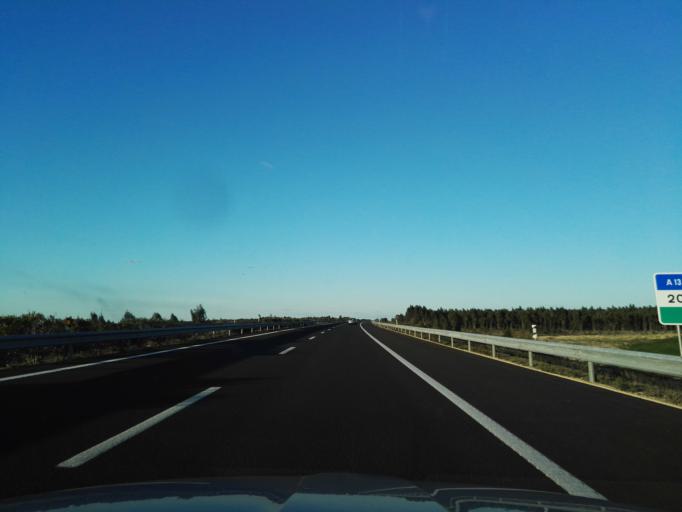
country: PT
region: Santarem
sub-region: Benavente
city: Poceirao
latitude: 38.7582
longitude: -8.6840
